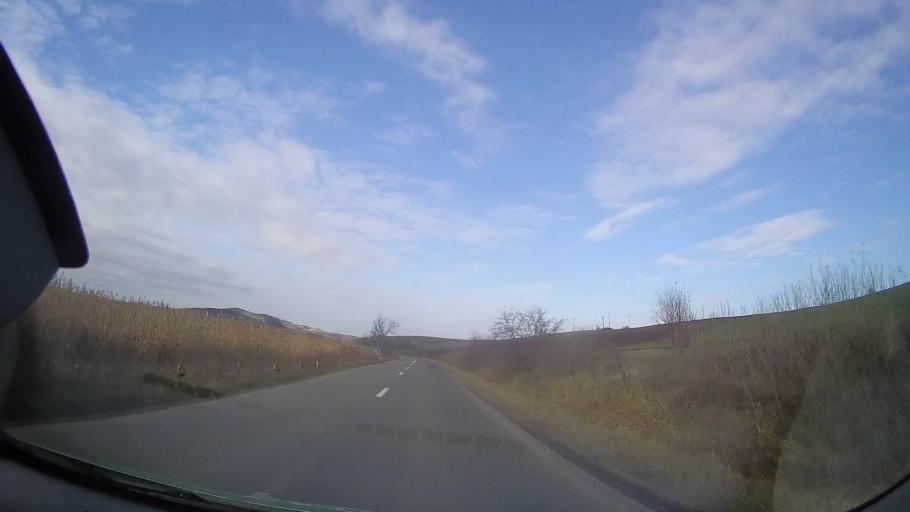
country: RO
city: Barza
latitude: 46.5636
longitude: 24.0974
